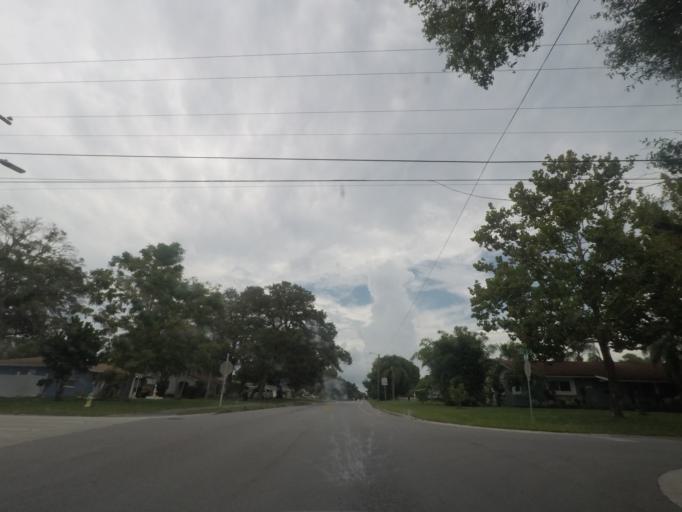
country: US
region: Florida
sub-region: Pinellas County
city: Kenneth City
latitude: 27.7990
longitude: -82.7043
